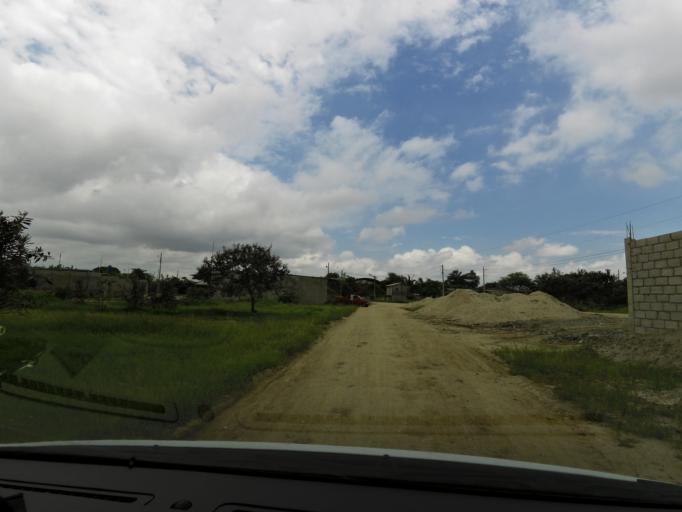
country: EC
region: El Oro
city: Huaquillas
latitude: -3.4828
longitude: -80.2049
